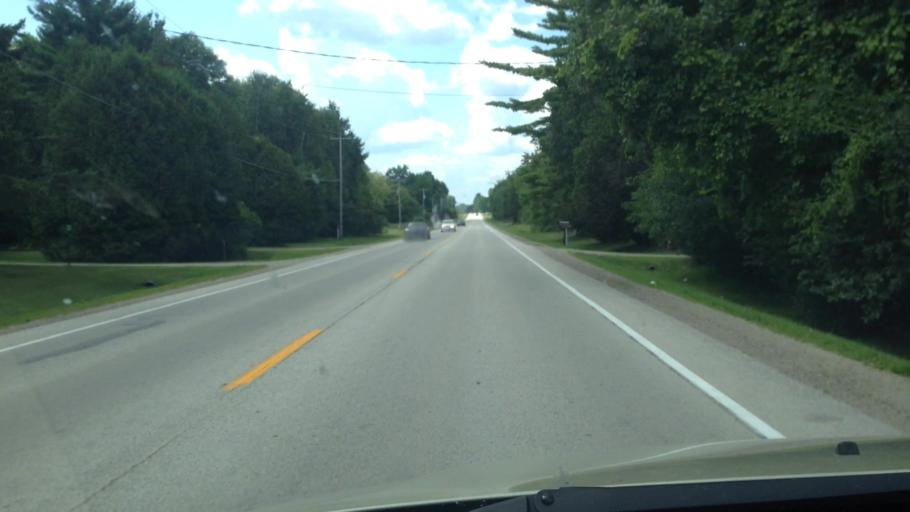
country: US
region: Wisconsin
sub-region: Brown County
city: Suamico
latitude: 44.6398
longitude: -88.0743
